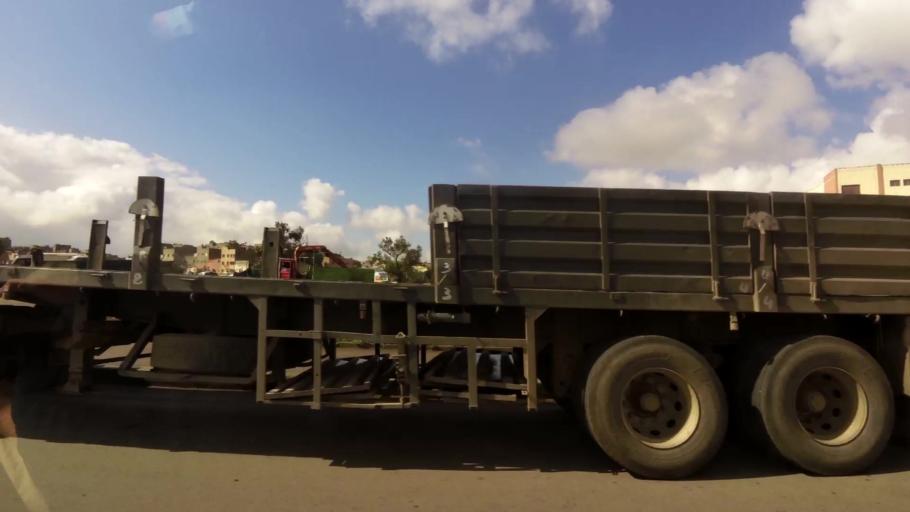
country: MA
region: Grand Casablanca
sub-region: Nouaceur
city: Bouskoura
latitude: 33.5311
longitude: -7.6761
